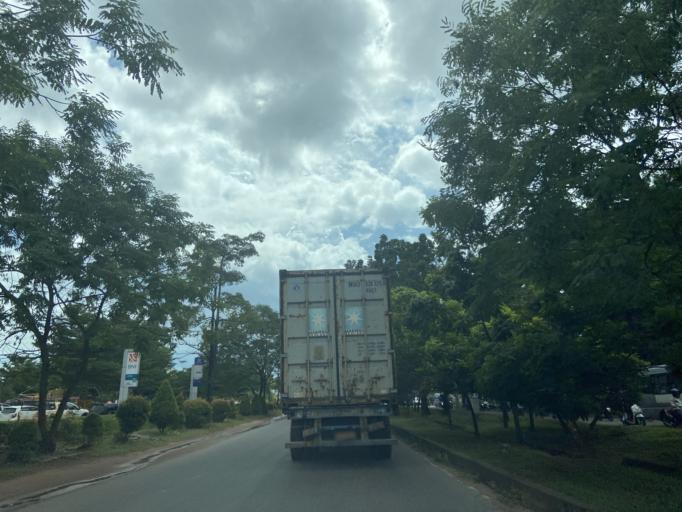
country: SG
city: Singapore
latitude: 1.0428
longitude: 103.9817
